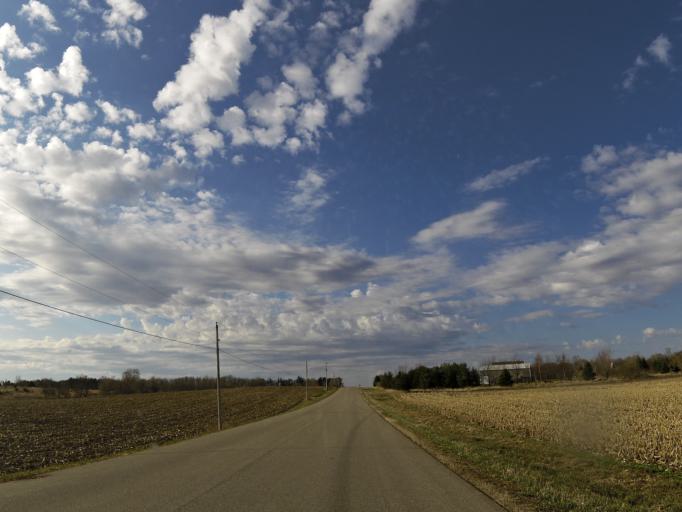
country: US
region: Minnesota
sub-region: Dakota County
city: Hastings
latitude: 44.7930
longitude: -92.8425
